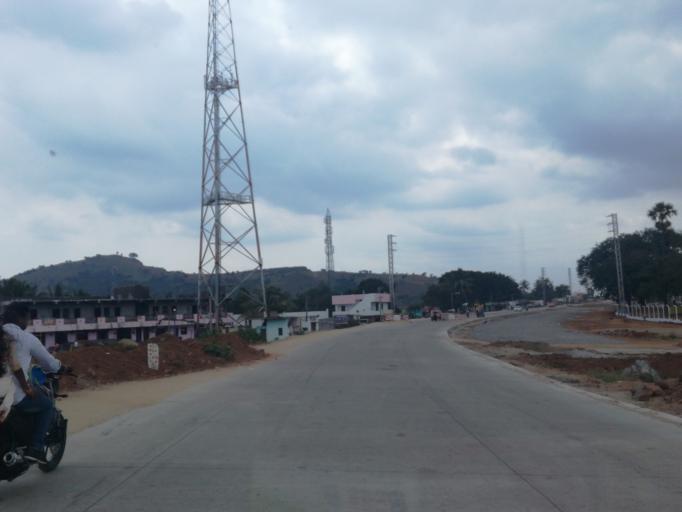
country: IN
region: Andhra Pradesh
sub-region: Chittoor
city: Ramapuram
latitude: 13.0943
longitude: 79.1328
